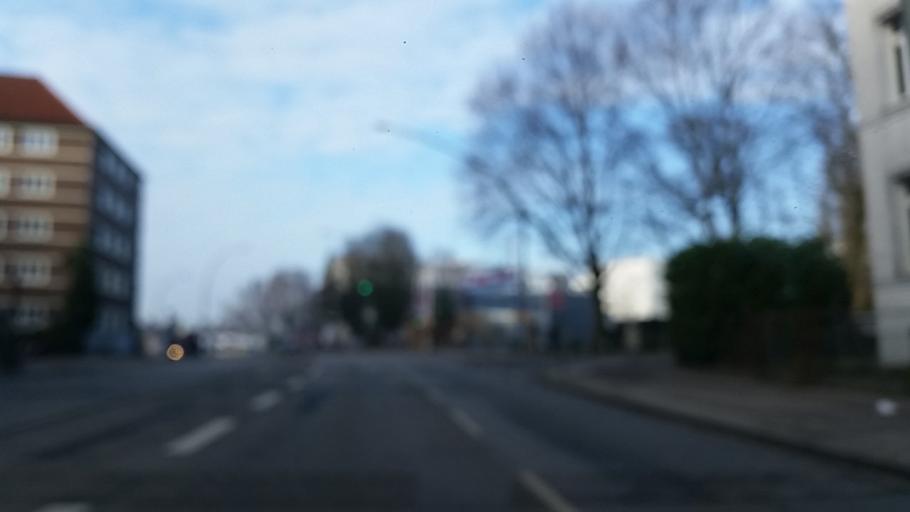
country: DE
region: Hamburg
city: Hamburg-Nord
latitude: 53.5975
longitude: 9.9789
